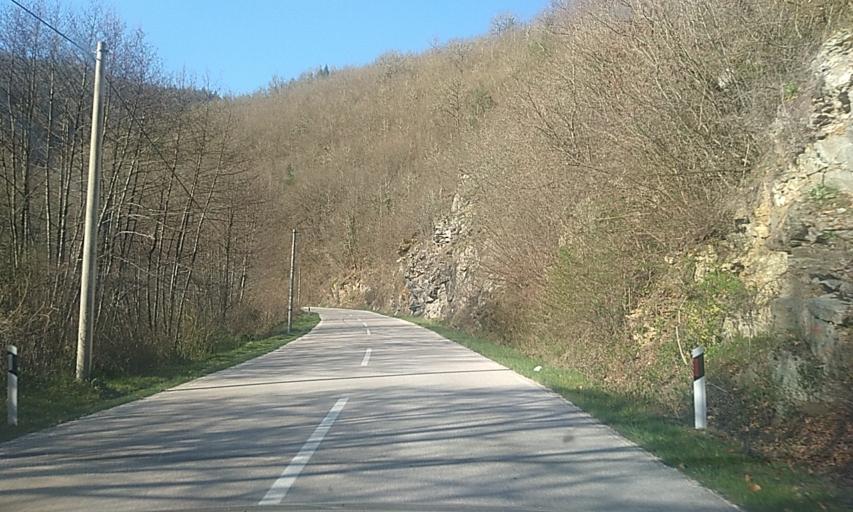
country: RS
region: Central Serbia
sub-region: Pcinjski Okrug
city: Bosilegrad
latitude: 42.4345
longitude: 22.5127
